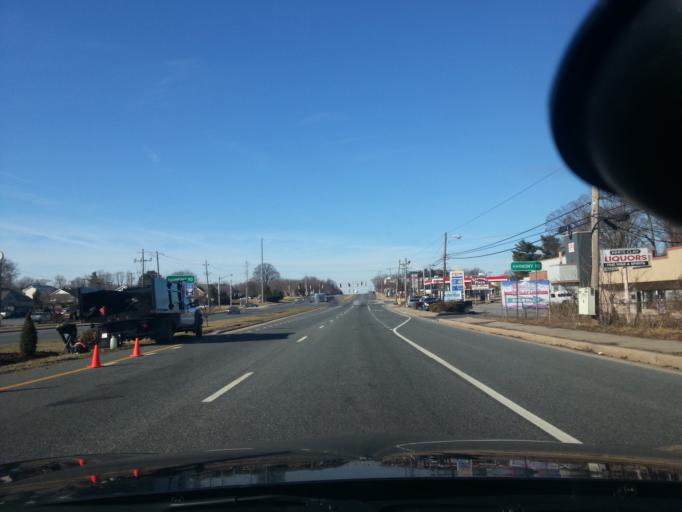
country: US
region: Delaware
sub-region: New Castle County
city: Pike Creek
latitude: 39.6865
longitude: -75.6801
